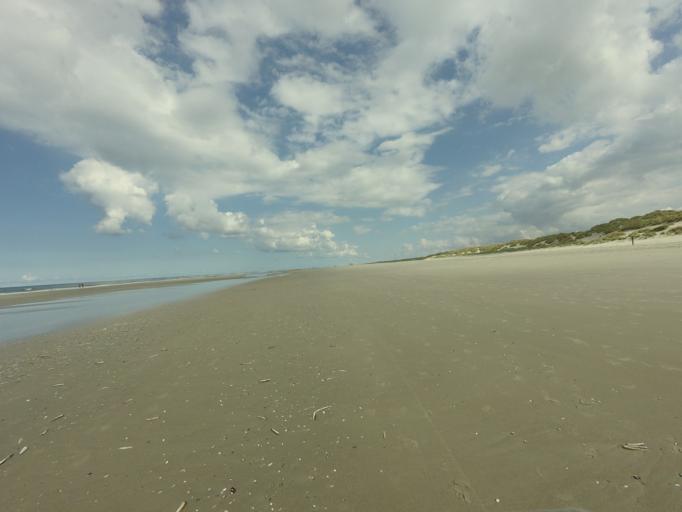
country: NL
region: Friesland
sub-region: Gemeente Terschelling
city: West-Terschelling
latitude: 53.4013
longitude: 5.2370
